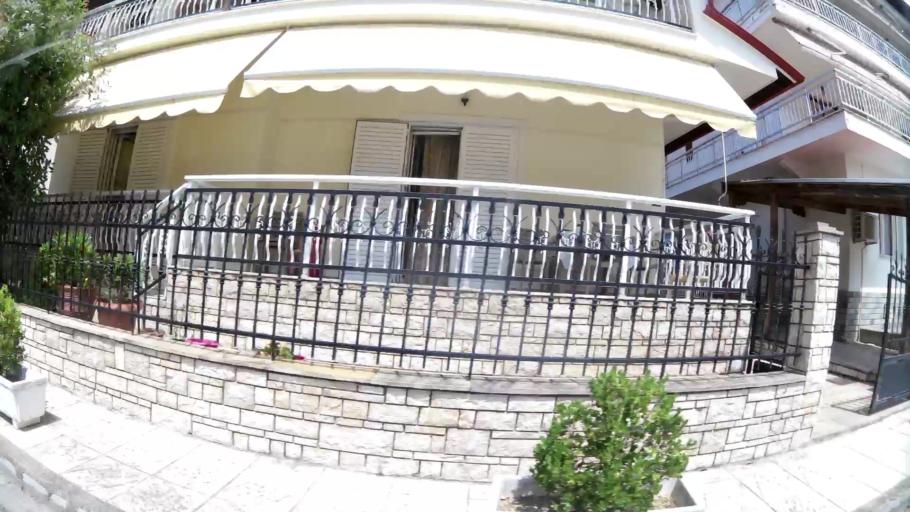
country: GR
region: Central Macedonia
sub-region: Nomos Pierias
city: Katerini
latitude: 40.2646
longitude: 22.5045
